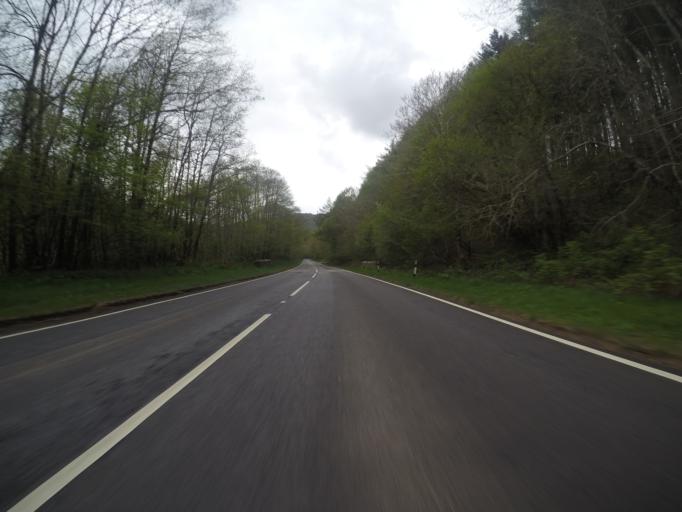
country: GB
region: Scotland
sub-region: Highland
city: Beauly
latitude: 57.2205
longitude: -4.6357
